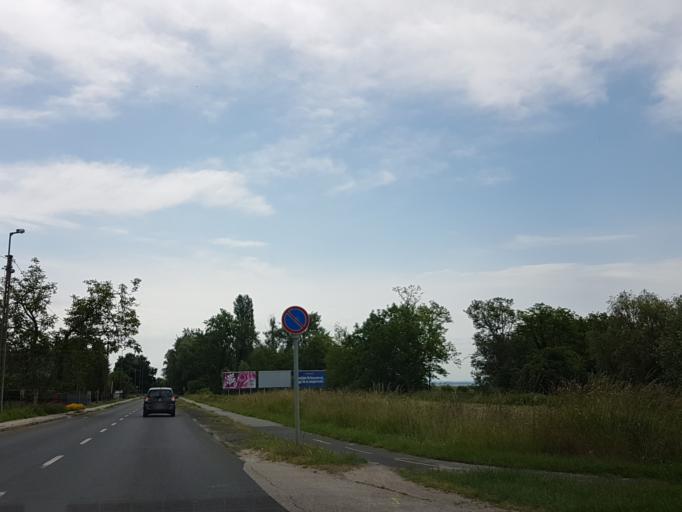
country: HU
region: Veszprem
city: Badacsonytomaj
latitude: 46.8063
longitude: 17.5313
